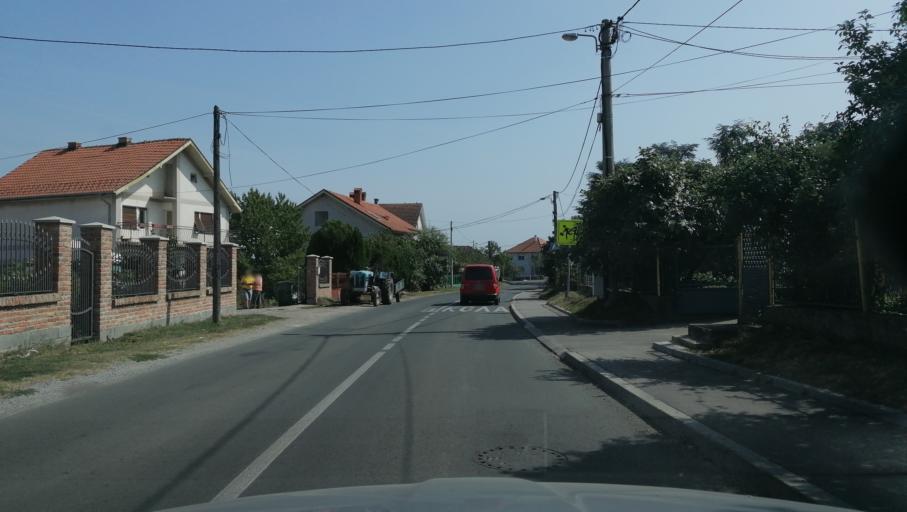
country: RS
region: Central Serbia
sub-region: Belgrade
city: Zvezdara
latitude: 44.7016
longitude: 20.5539
